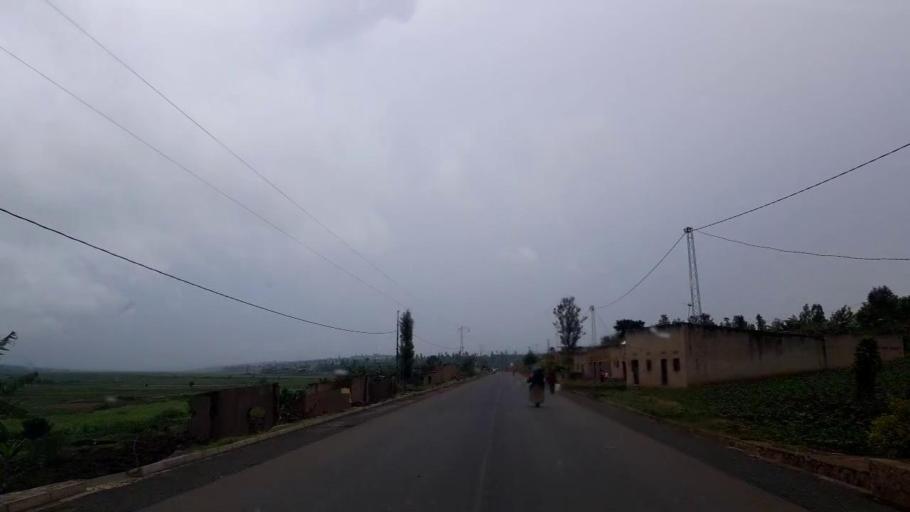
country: RW
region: Northern Province
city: Byumba
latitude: -1.4170
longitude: 30.2795
